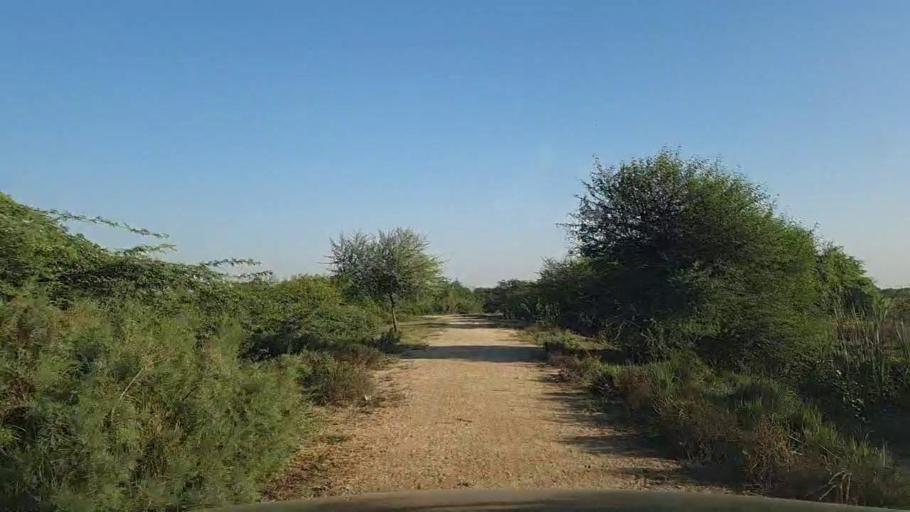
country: PK
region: Sindh
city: Mirpur Batoro
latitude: 24.6812
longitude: 68.3647
